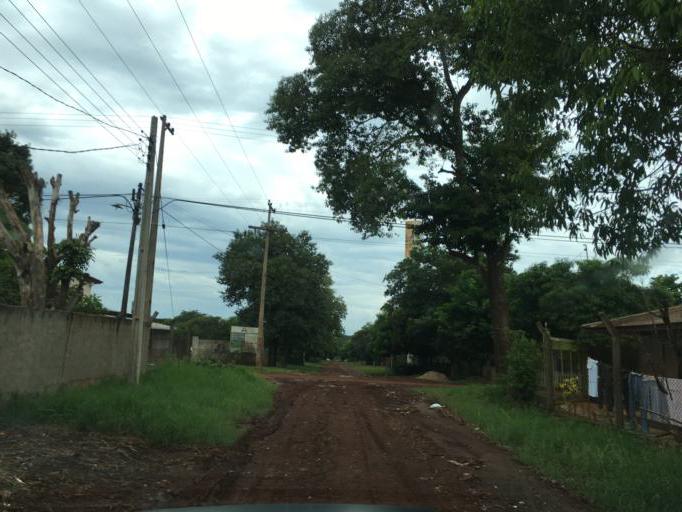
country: PY
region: Alto Parana
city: Ciudad del Este
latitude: -25.4208
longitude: -54.6400
